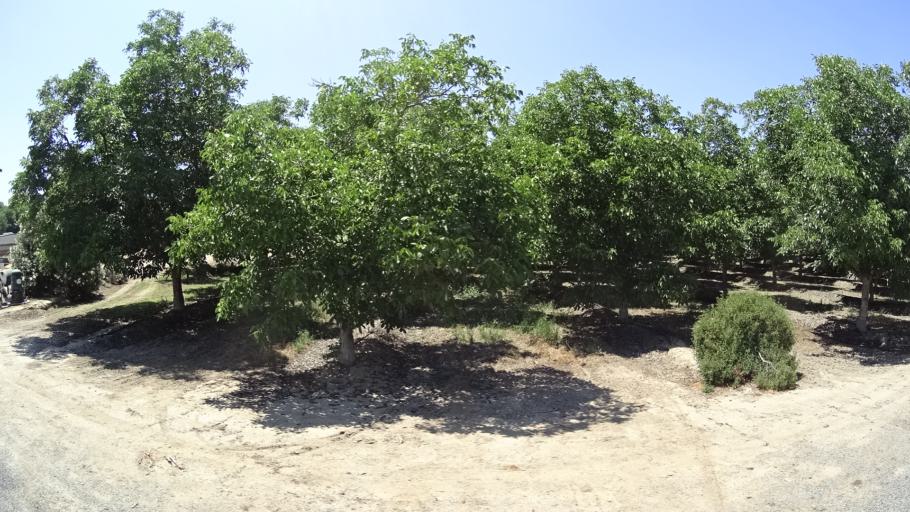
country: US
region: California
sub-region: Fresno County
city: Laton
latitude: 36.4088
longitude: -119.6954
